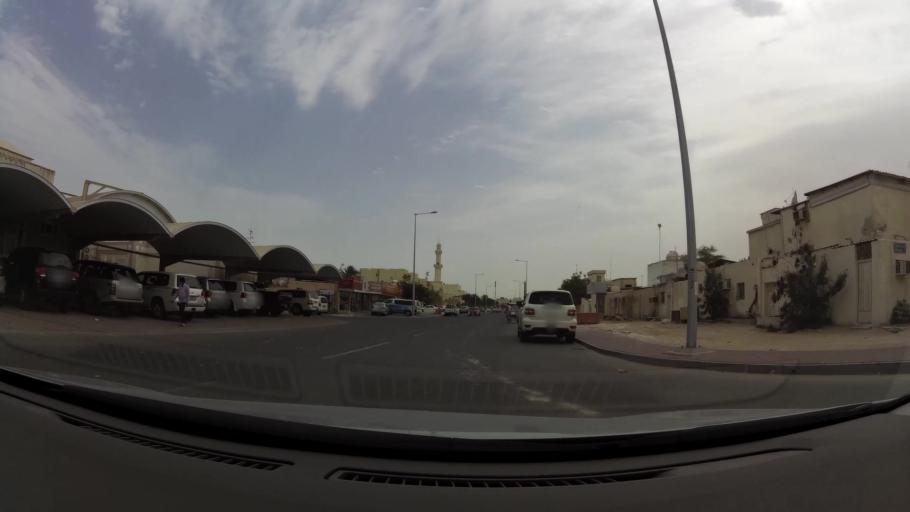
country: QA
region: Baladiyat ar Rayyan
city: Ar Rayyan
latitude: 25.3258
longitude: 51.4696
